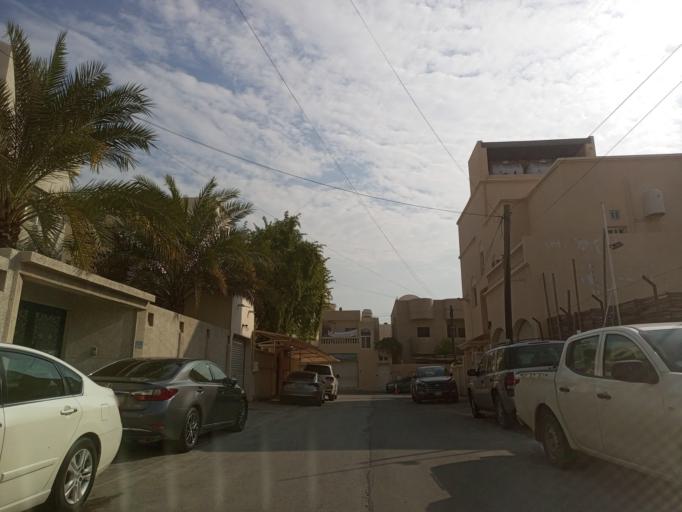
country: BH
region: Muharraq
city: Al Hadd
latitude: 26.2506
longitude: 50.6433
